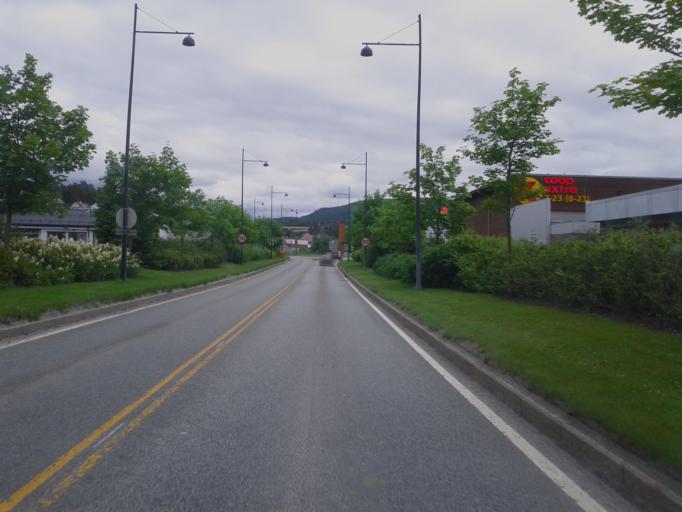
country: NO
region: Nord-Trondelag
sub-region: Steinkjer
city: Steinkjer
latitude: 64.0221
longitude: 11.4889
